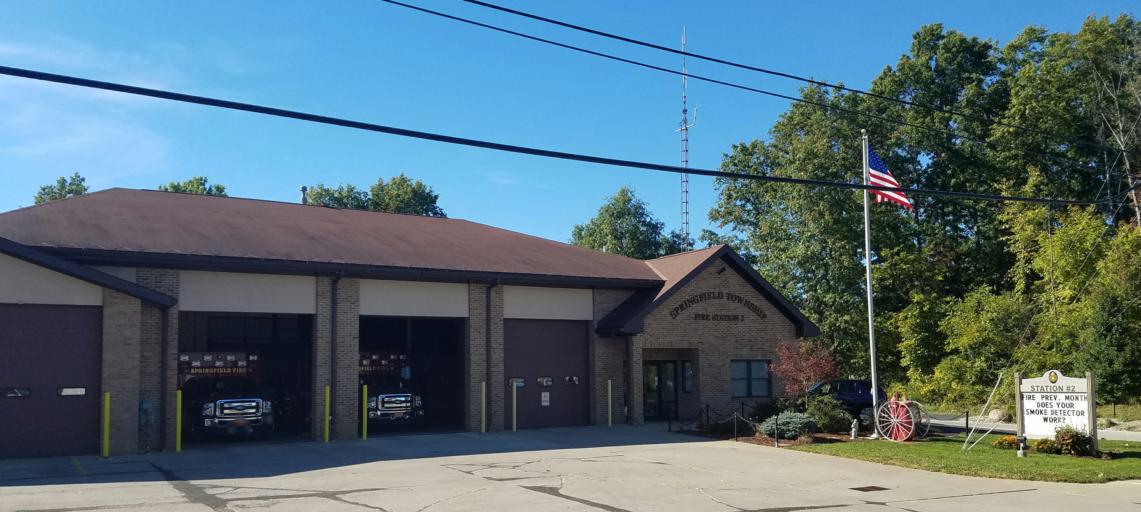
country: US
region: Ohio
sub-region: Richland County
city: Ontario
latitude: 40.7482
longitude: -82.5898
